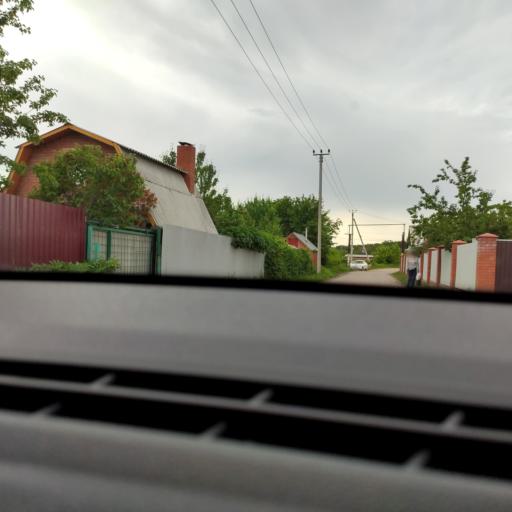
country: RU
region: Samara
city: Podstepki
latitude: 53.5125
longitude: 49.0717
